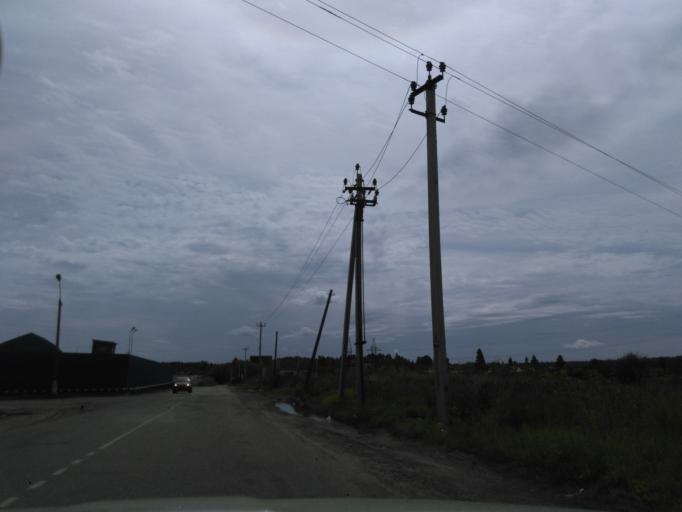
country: RU
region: Moskovskaya
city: Solnechnogorsk
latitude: 56.1650
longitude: 36.9881
